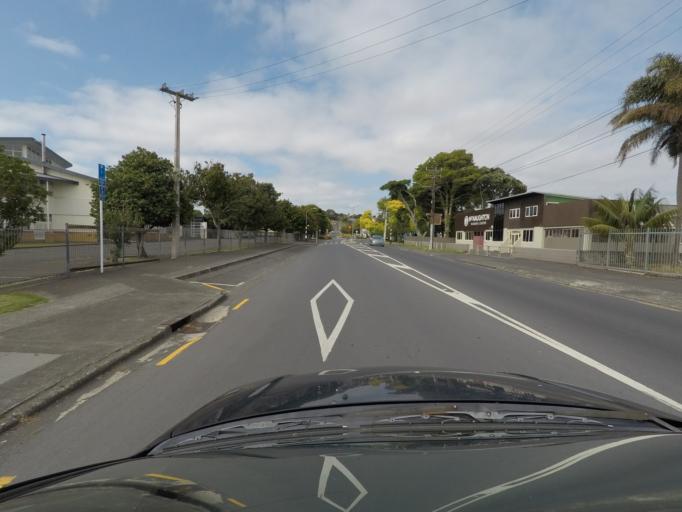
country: NZ
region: Auckland
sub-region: Auckland
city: Auckland
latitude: -36.9128
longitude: 174.7477
